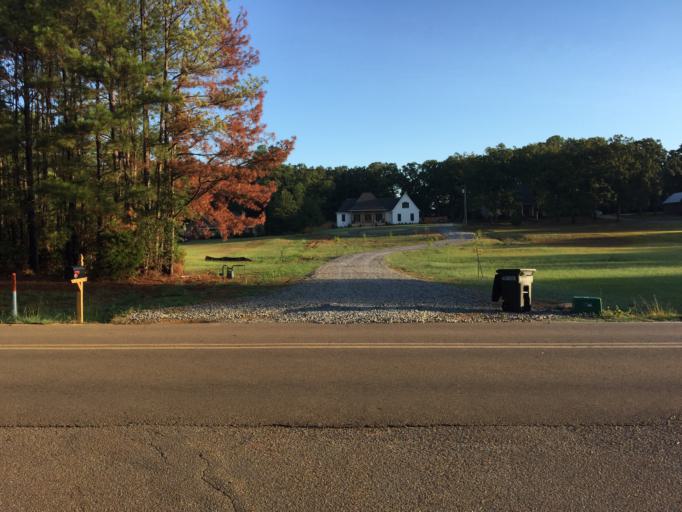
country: US
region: Mississippi
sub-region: Madison County
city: Madison
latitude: 32.4650
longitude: -90.0672
